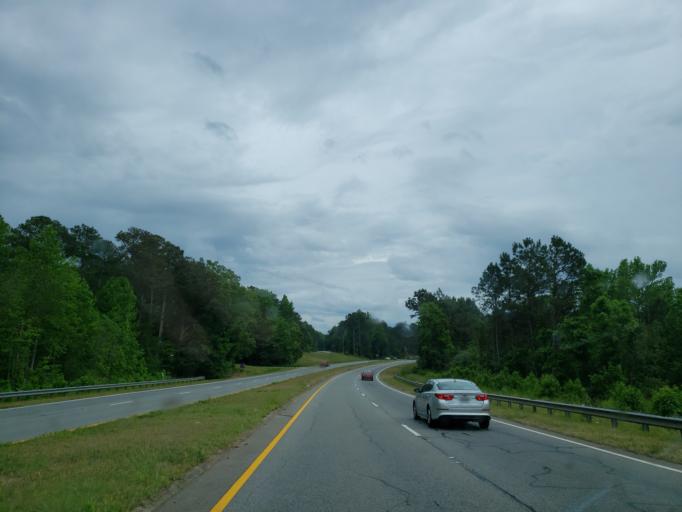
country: US
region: Georgia
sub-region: Haralson County
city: Bremen
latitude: 33.7561
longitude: -85.1610
